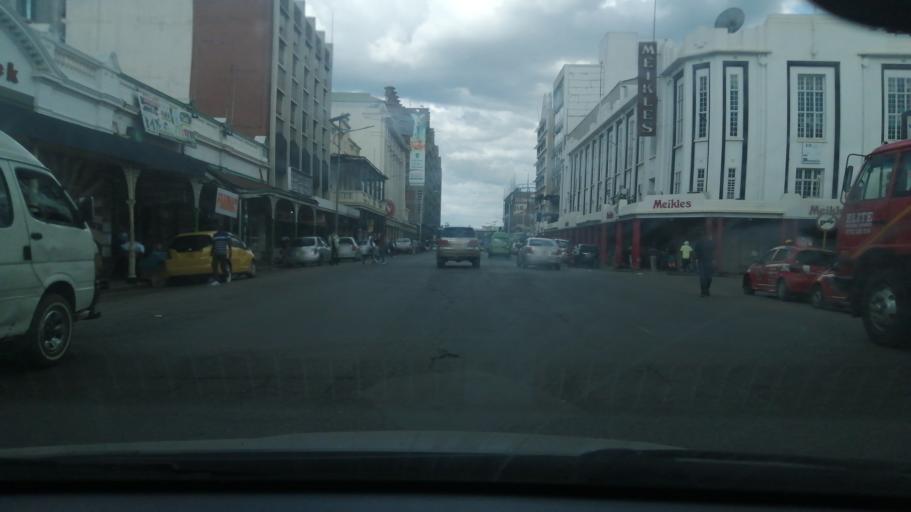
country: ZW
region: Harare
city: Harare
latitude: -17.8324
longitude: 31.0504
